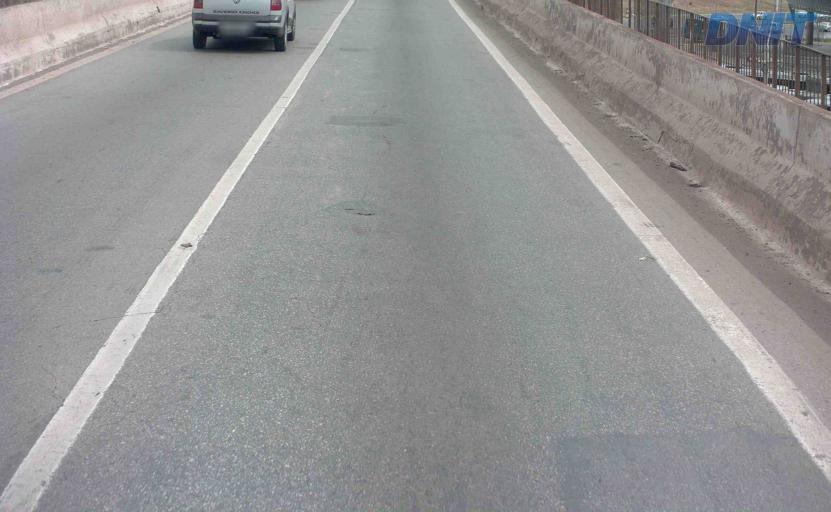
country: BR
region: Minas Gerais
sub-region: Belo Horizonte
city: Belo Horizonte
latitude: -19.8641
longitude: -43.9260
